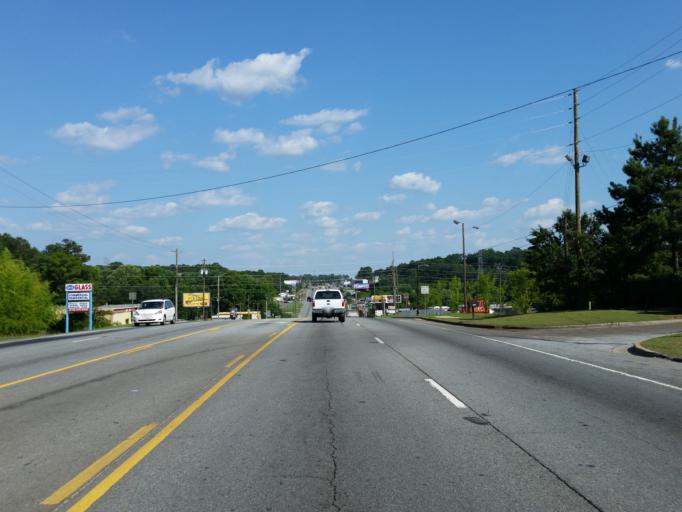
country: US
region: Georgia
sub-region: Cobb County
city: Marietta
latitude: 33.9662
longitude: -84.5346
